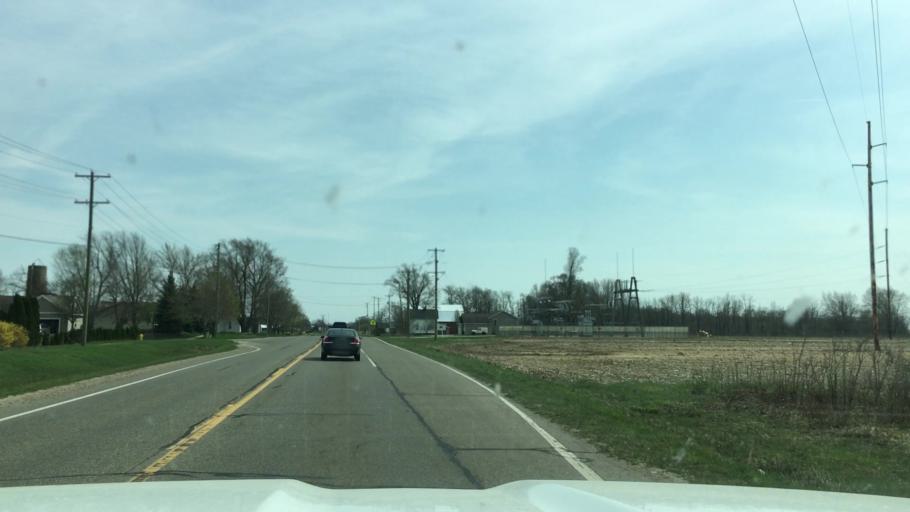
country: US
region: Michigan
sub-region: Ottawa County
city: Hudsonville
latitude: 42.8817
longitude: -85.9014
